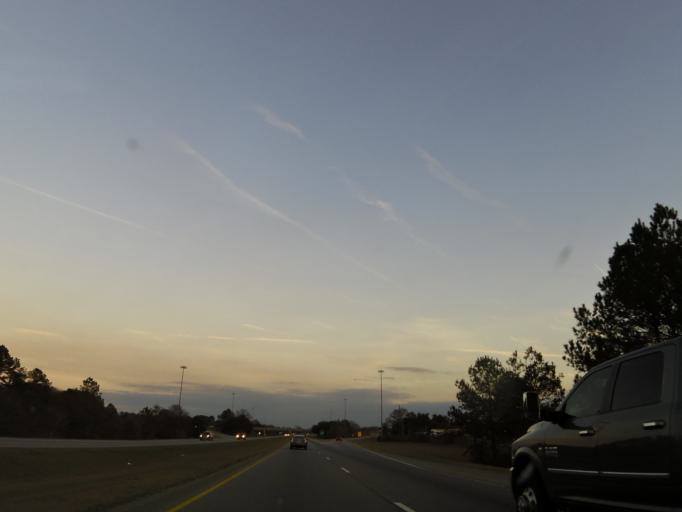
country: US
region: Georgia
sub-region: Dougherty County
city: Albany
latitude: 31.5932
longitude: -84.1301
